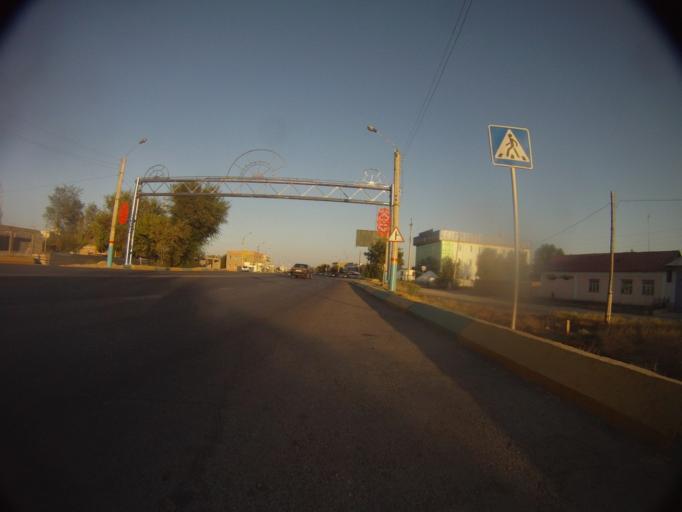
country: KZ
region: Ongtustik Qazaqstan
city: Turkestan
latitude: 43.2893
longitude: 68.2949
